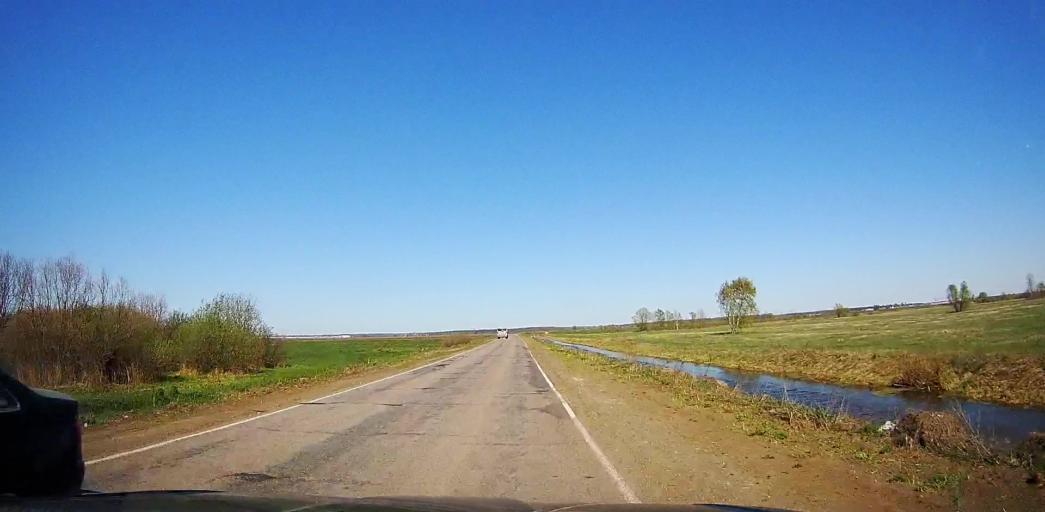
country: RU
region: Moskovskaya
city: Ramenskoye
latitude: 55.5040
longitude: 38.2475
